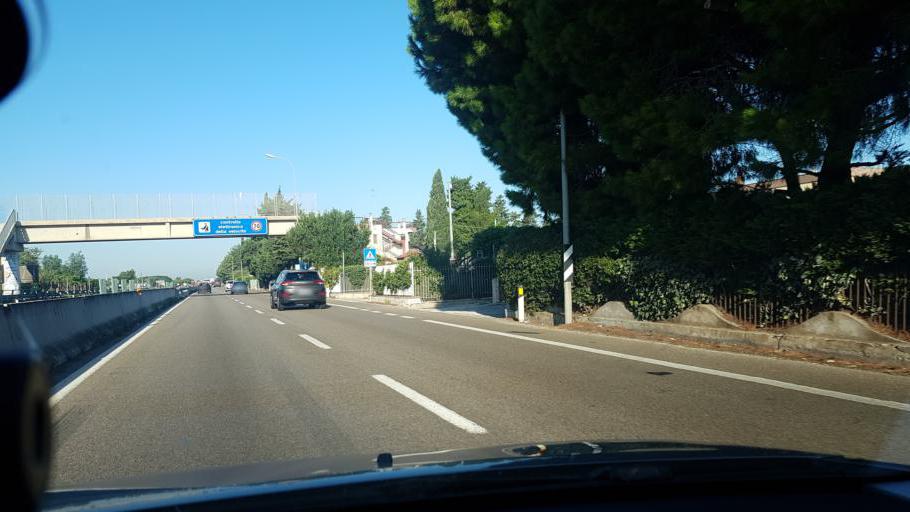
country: IT
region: Apulia
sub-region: Provincia di Bari
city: Parco Scizzo-Parchitello
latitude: 41.0894
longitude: 16.9772
